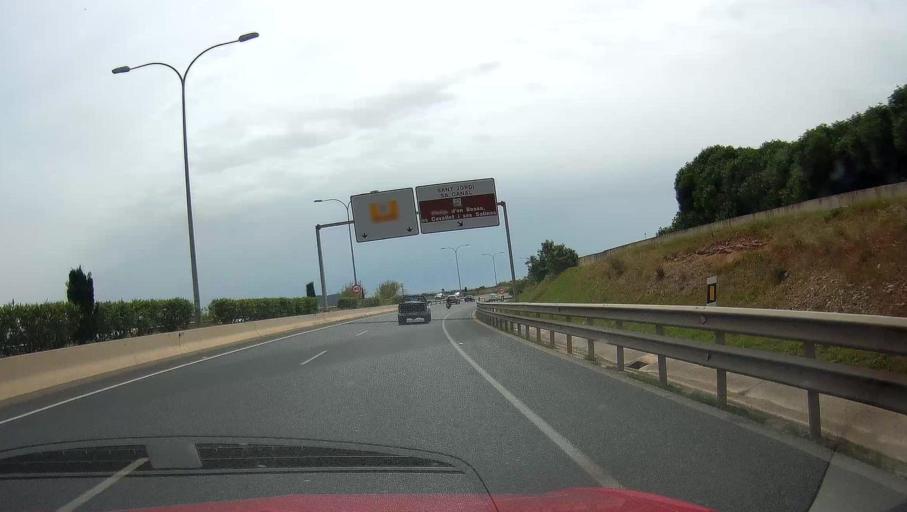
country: ES
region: Balearic Islands
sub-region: Illes Balears
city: Ibiza
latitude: 38.8894
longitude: 1.4000
